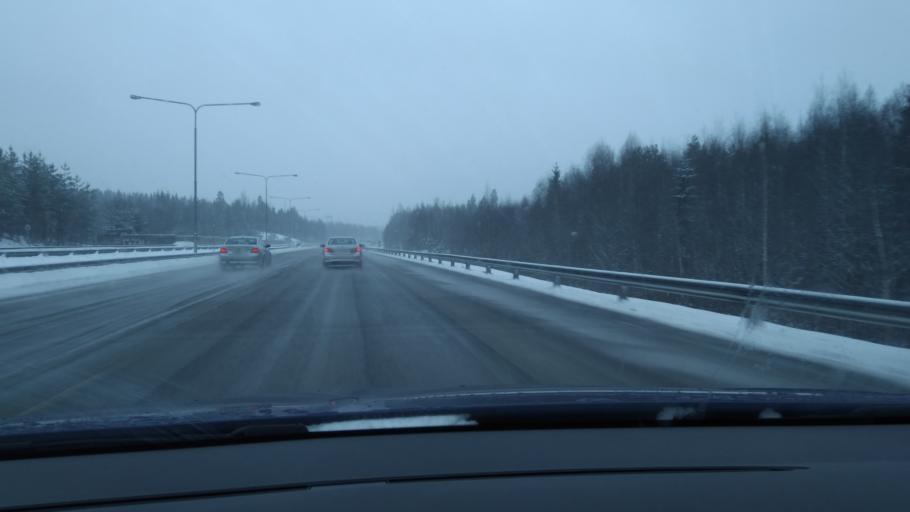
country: FI
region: Pirkanmaa
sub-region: Tampere
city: Tampere
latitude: 61.5038
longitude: 23.8961
